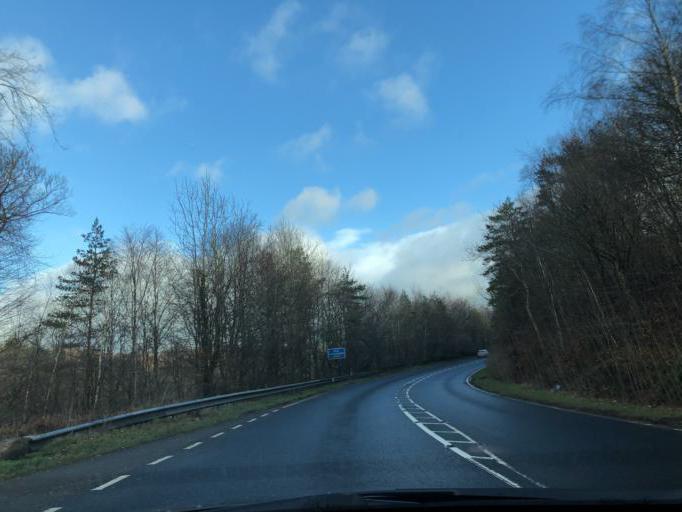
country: GB
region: England
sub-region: Cumbria
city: Grange-over-Sands
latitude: 54.2622
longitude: -2.9874
